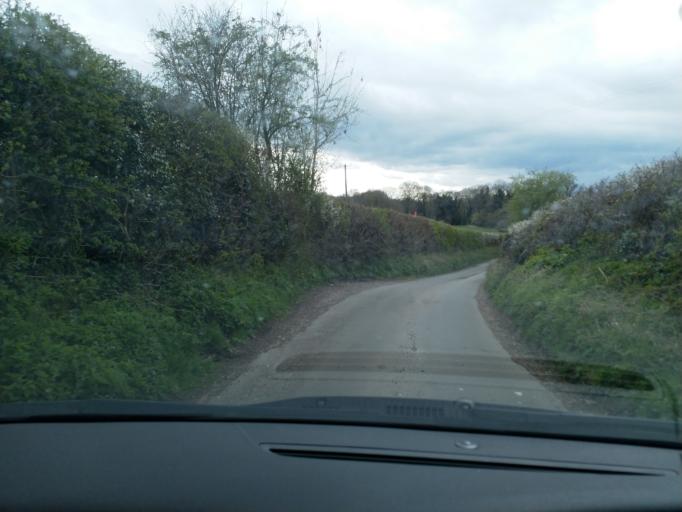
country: GB
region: England
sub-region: Warwickshire
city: Henley in Arden
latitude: 52.2911
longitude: -1.7450
